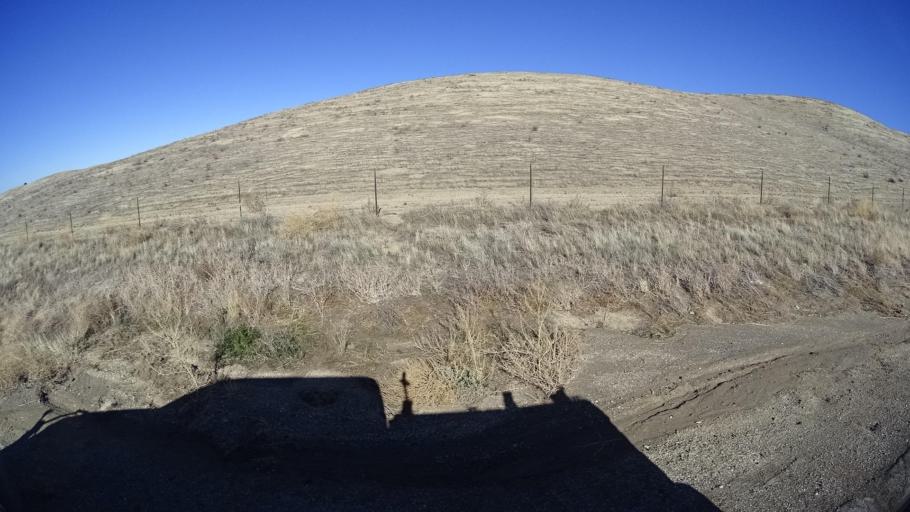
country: US
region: California
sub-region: Kern County
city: Maricopa
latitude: 34.9479
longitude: -119.4179
